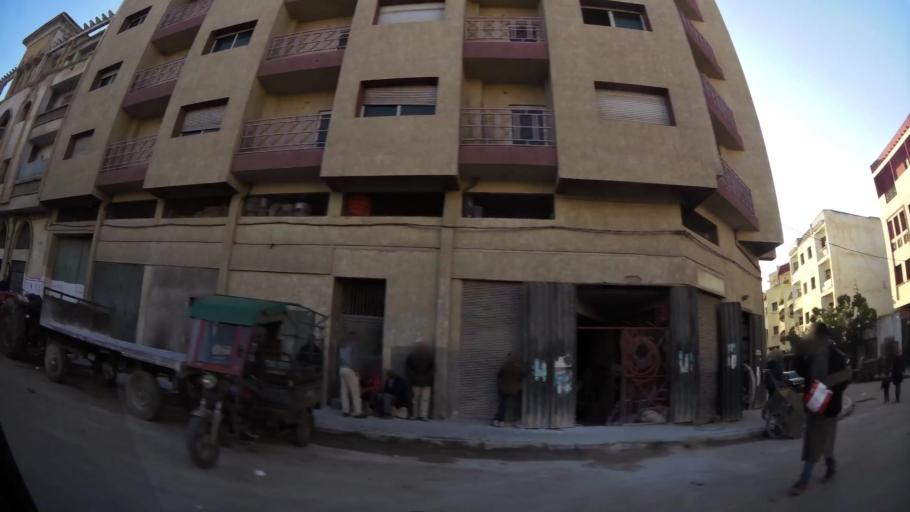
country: MA
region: Chaouia-Ouardigha
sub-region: Settat Province
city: Settat
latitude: 33.0021
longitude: -7.6158
